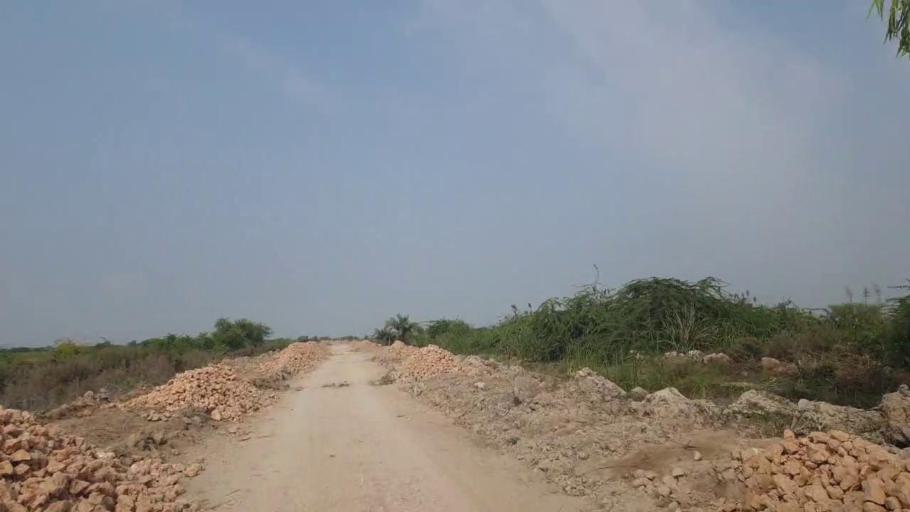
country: PK
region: Sindh
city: Badin
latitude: 24.6066
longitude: 68.7417
